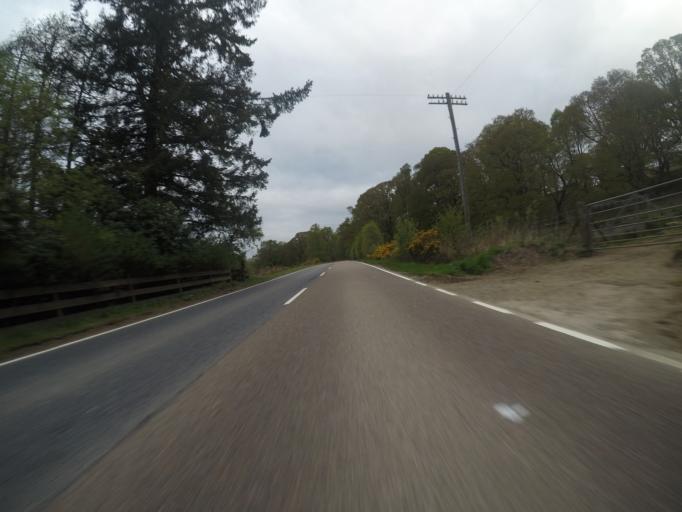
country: GB
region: Scotland
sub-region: Highland
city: Spean Bridge
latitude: 56.8936
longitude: -4.8871
